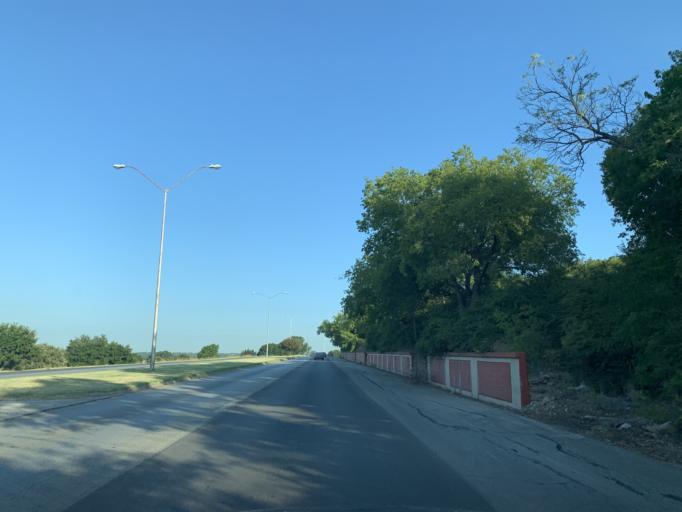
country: US
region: Texas
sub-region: Tarrant County
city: River Oaks
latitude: 32.7728
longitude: -97.3636
